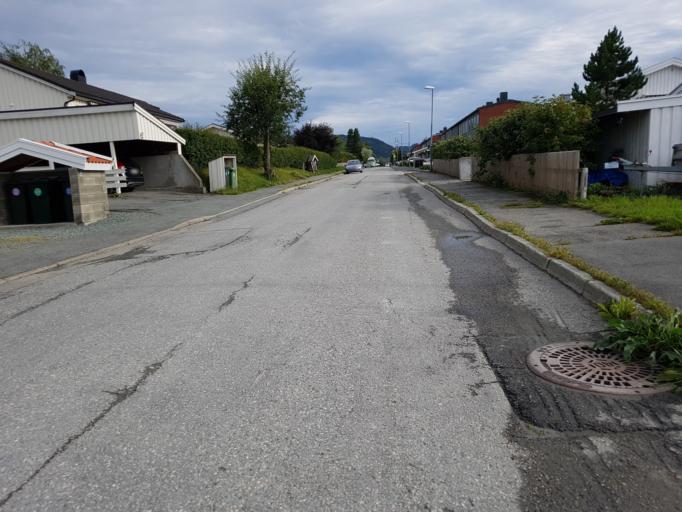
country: NO
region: Sor-Trondelag
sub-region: Trondheim
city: Trondheim
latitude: 63.3928
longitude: 10.4233
